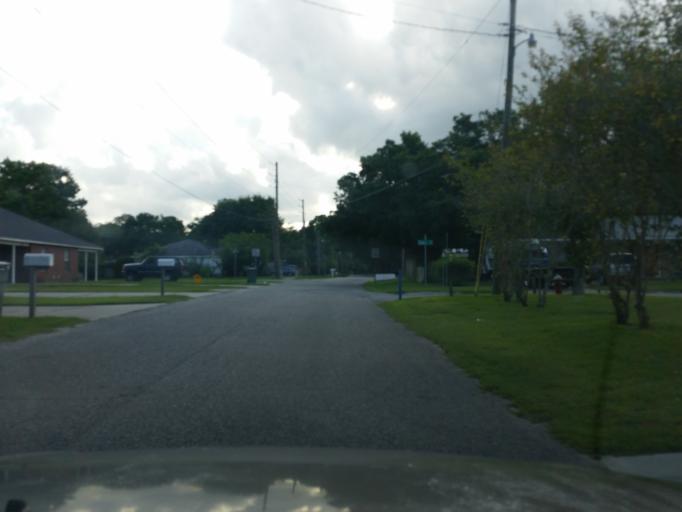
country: US
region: Florida
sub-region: Escambia County
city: Ferry Pass
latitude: 30.4993
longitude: -87.2135
